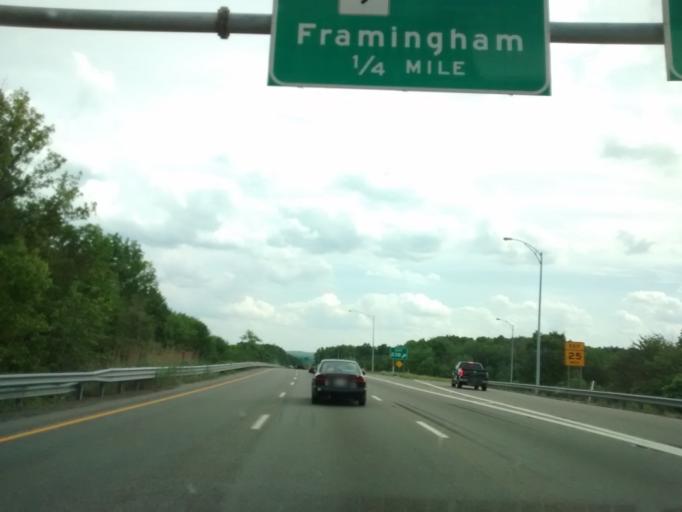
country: US
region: Massachusetts
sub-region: Worcester County
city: Southborough
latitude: 42.2921
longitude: -71.5681
